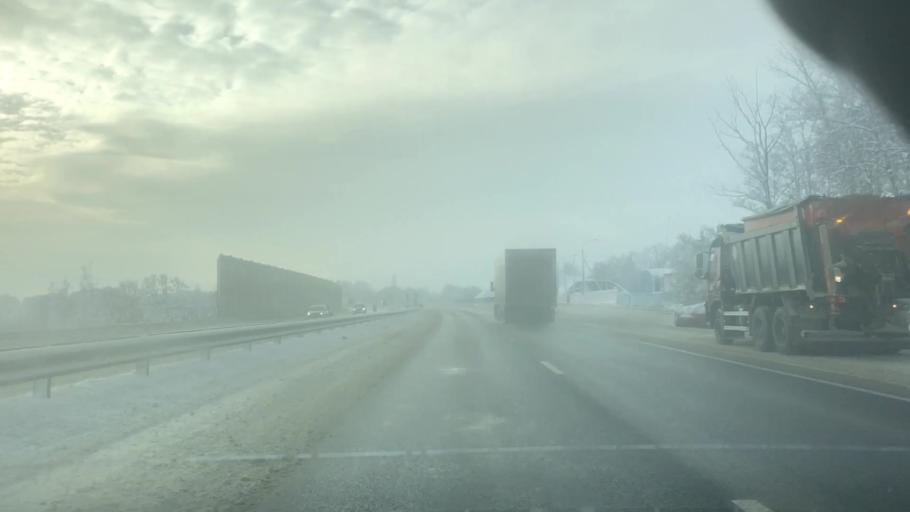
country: RU
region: Tula
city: Venev
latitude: 54.3941
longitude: 38.1561
